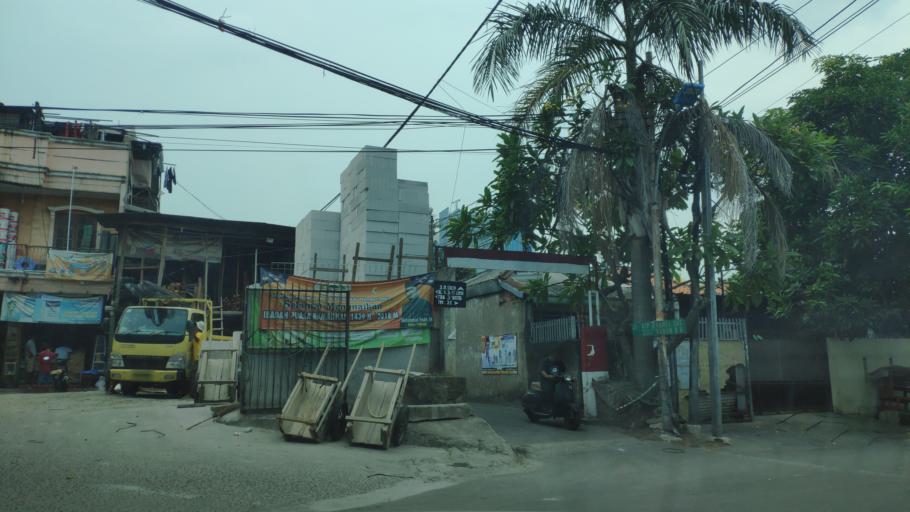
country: ID
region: Jakarta Raya
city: Jakarta
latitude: -6.1914
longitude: 106.8020
